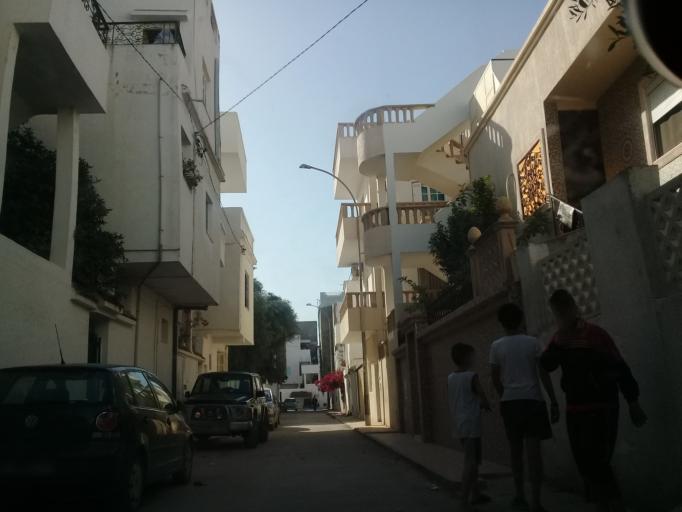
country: TN
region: Ariana
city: Ariana
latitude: 36.8333
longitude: 10.1938
